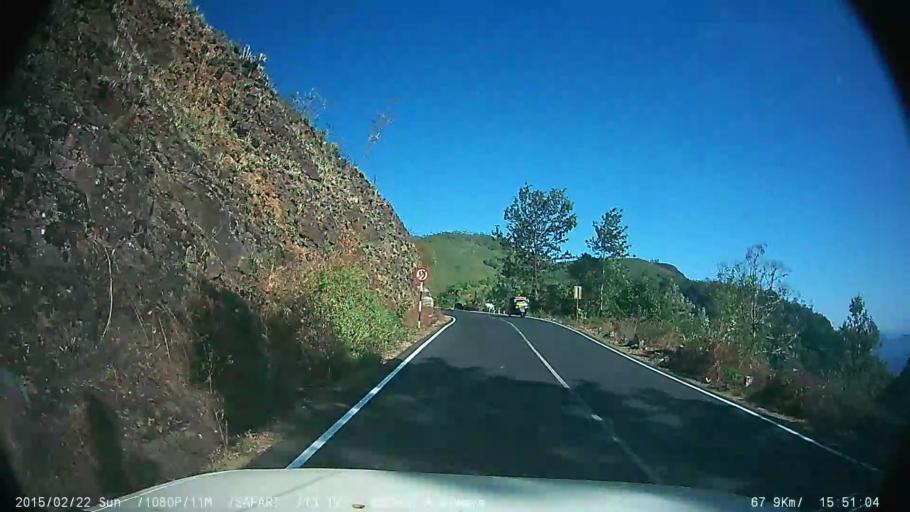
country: IN
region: Kerala
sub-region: Kottayam
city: Erattupetta
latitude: 9.5685
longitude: 77.0067
